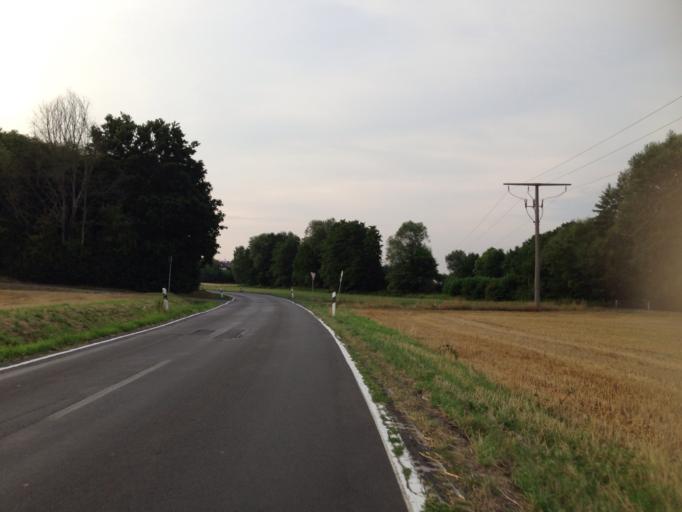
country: DE
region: Hesse
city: Allendorf an der Lahn
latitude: 50.5540
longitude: 8.6148
